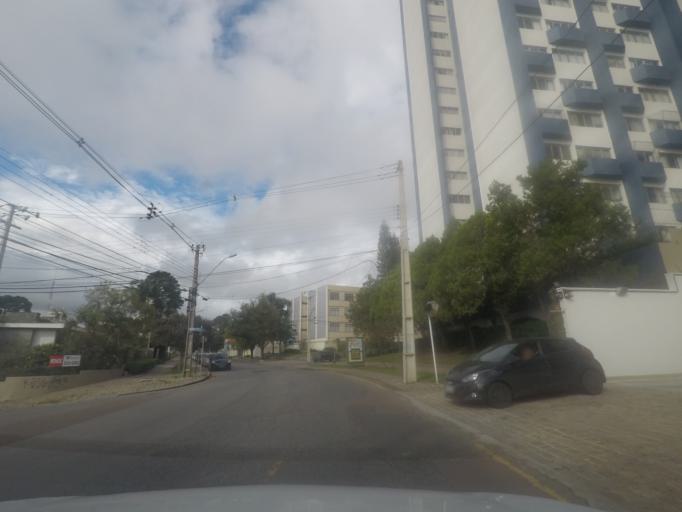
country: BR
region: Parana
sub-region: Curitiba
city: Curitiba
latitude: -25.4353
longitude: -49.2423
